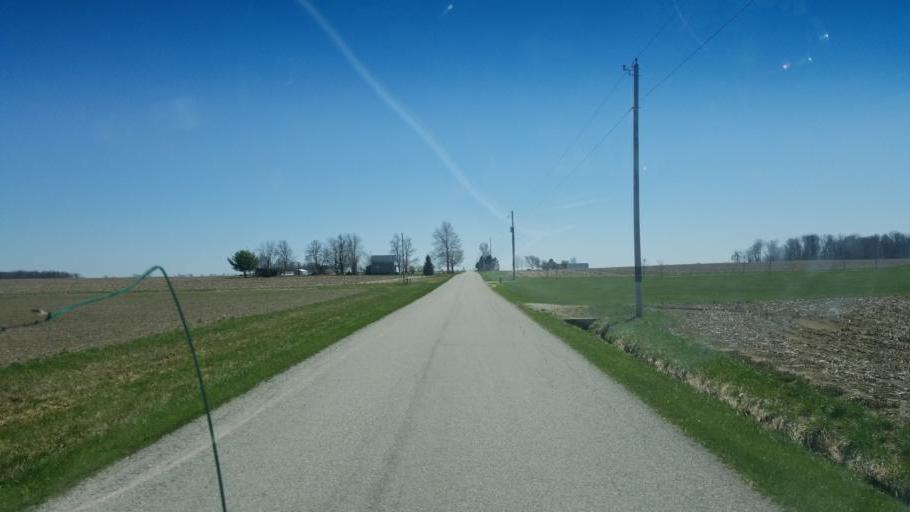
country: US
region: Ohio
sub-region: Huron County
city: Willard
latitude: 41.0633
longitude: -82.8424
